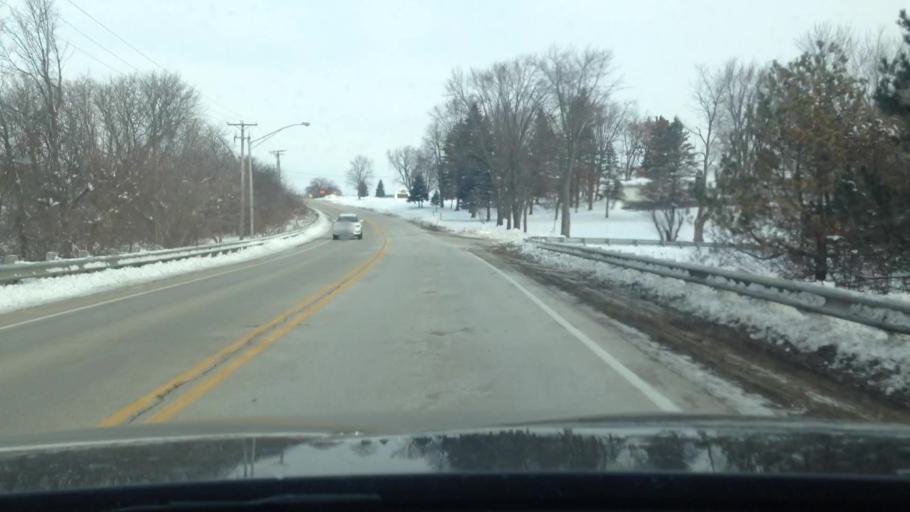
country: US
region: Illinois
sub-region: McHenry County
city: Woodstock
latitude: 42.3535
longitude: -88.4432
